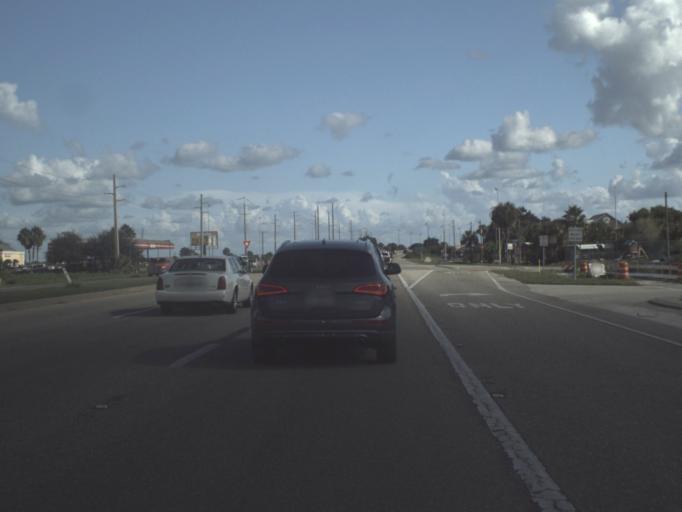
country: US
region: Florida
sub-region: Charlotte County
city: Charlotte Harbor
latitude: 26.9556
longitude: -82.0648
